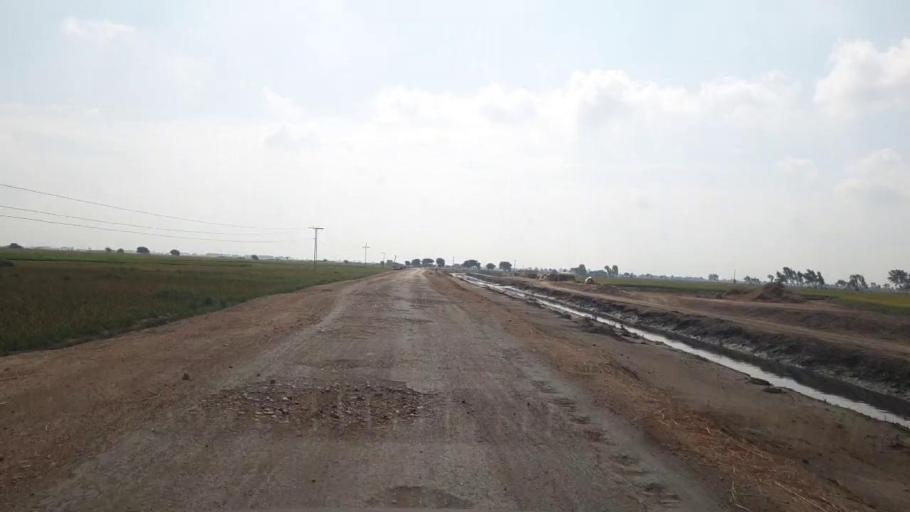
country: PK
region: Sindh
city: Kario
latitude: 24.6214
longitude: 68.5561
